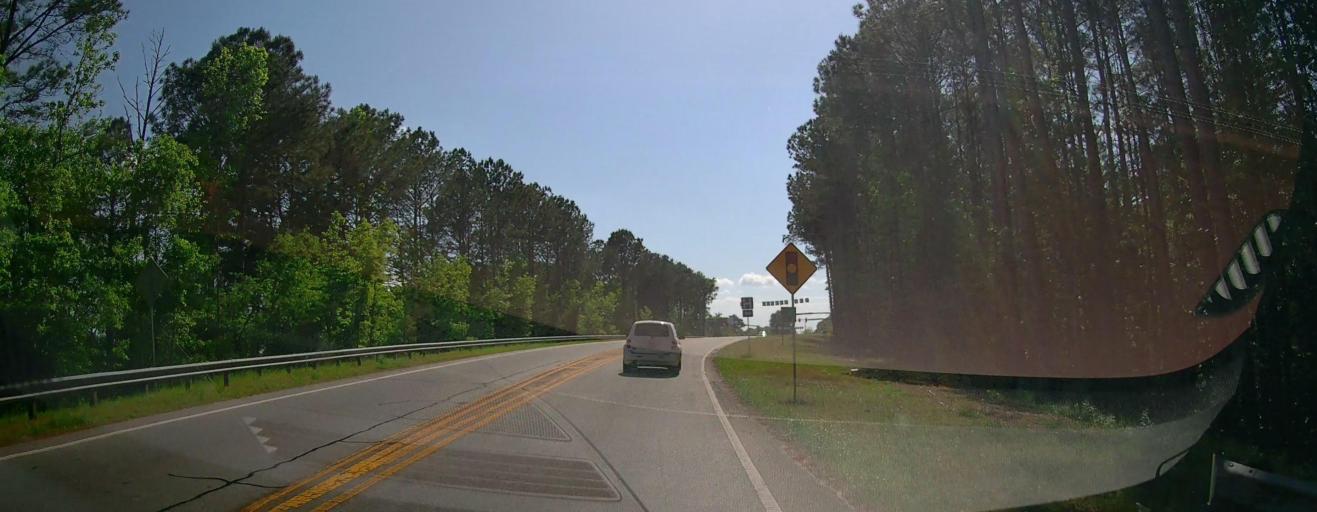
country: US
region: Georgia
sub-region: Morgan County
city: Madison
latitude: 33.6103
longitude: -83.4476
